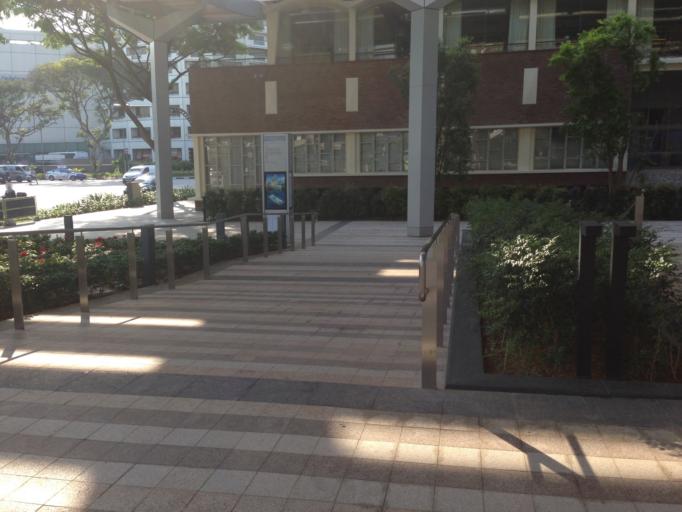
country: SG
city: Singapore
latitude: 1.2938
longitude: 103.8553
